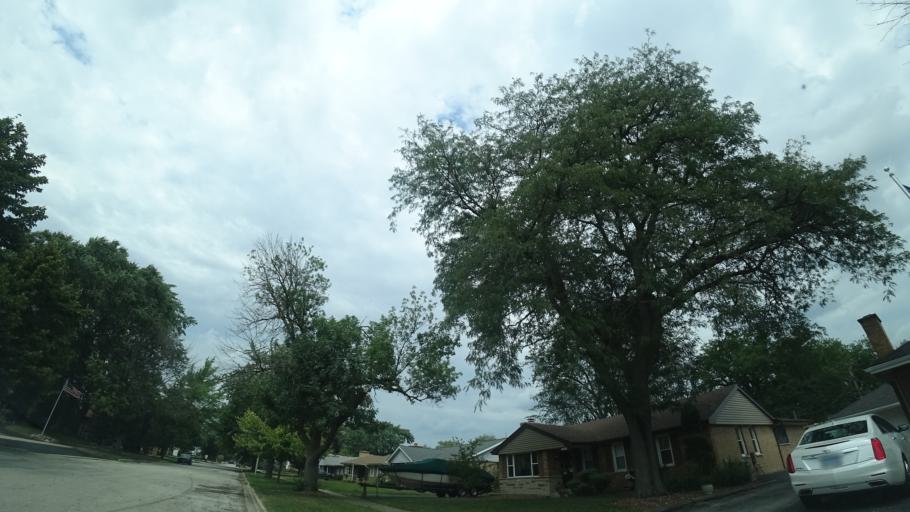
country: US
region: Illinois
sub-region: Cook County
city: Chicago Ridge
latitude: 41.6911
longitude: -87.7728
